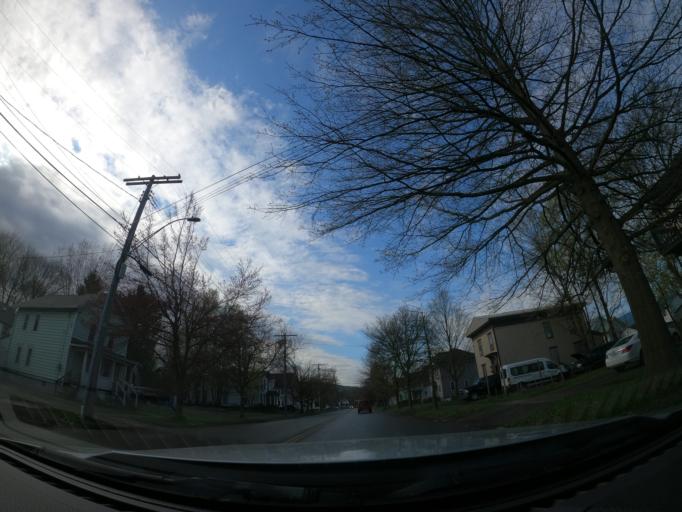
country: US
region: New York
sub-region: Cortland County
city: Cortland
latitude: 42.6004
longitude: -76.1669
